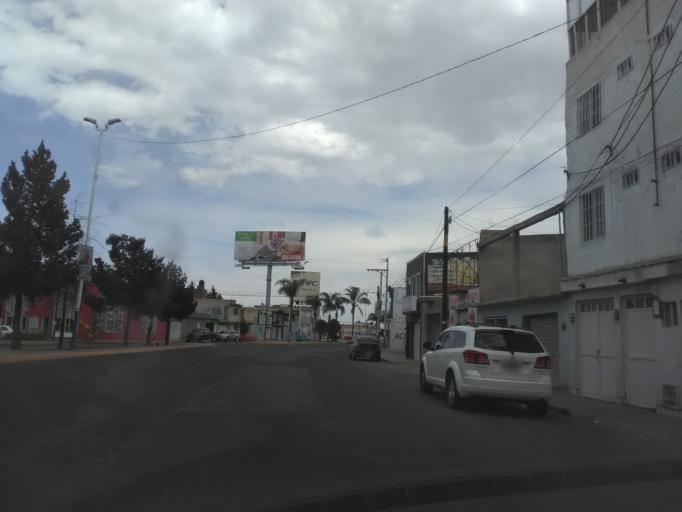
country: MX
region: Durango
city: Victoria de Durango
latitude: 24.0194
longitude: -104.6607
